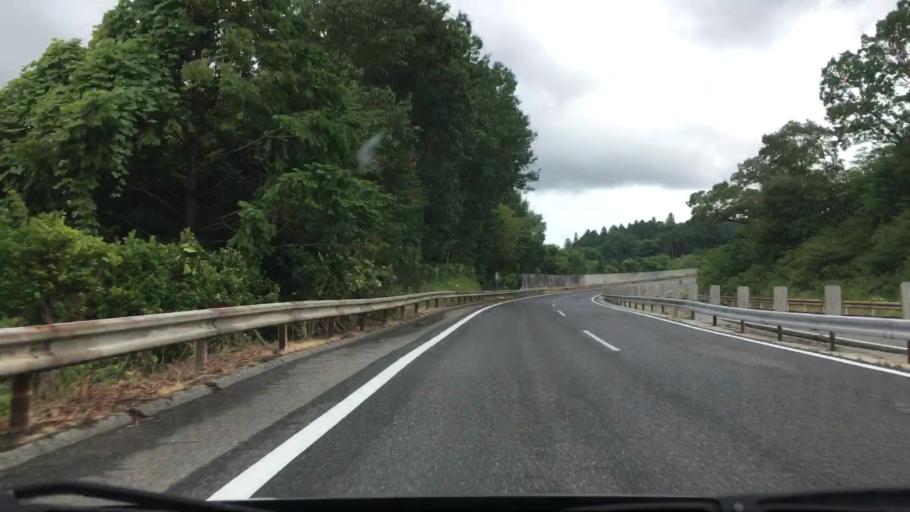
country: JP
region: Okayama
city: Niimi
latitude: 34.9138
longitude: 133.3121
